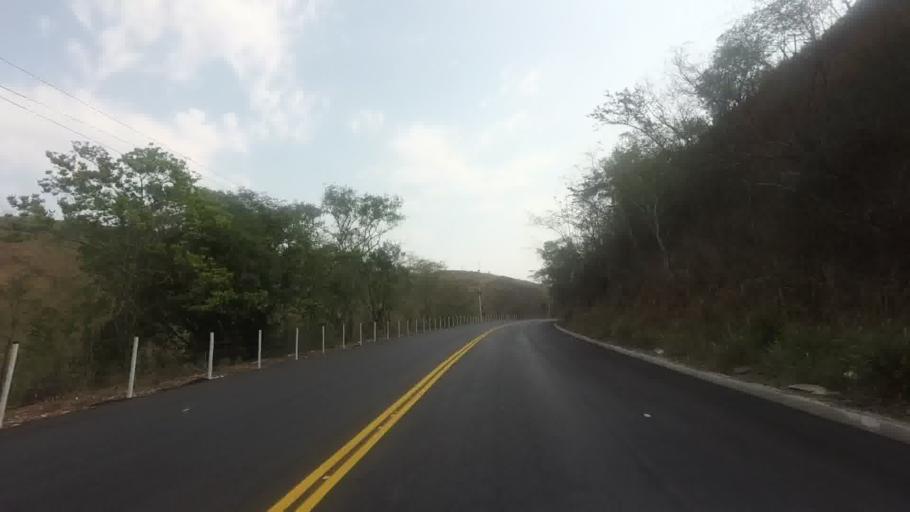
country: BR
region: Rio de Janeiro
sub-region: Itaperuna
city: Itaperuna
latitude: -21.2473
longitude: -41.7585
